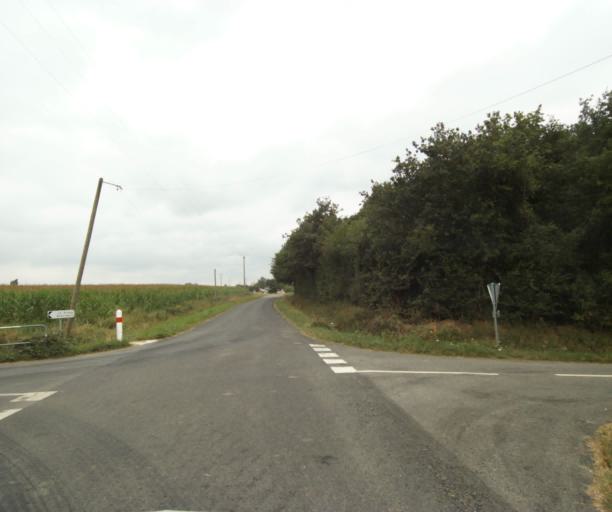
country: FR
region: Pays de la Loire
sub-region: Departement de la Sarthe
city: Solesmes
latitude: 47.8615
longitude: -0.3033
